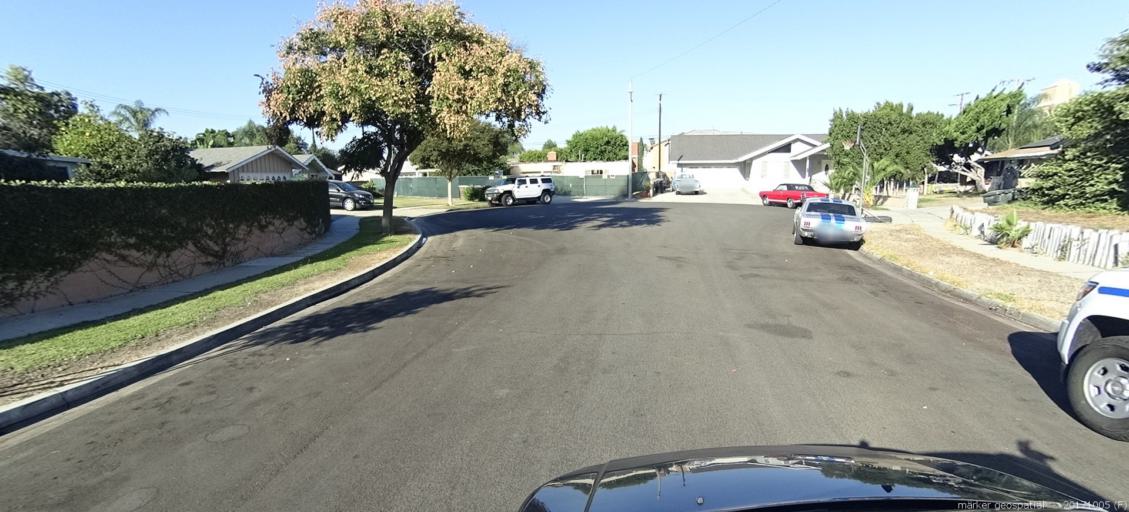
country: US
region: California
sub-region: Orange County
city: Garden Grove
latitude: 33.8021
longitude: -117.9493
